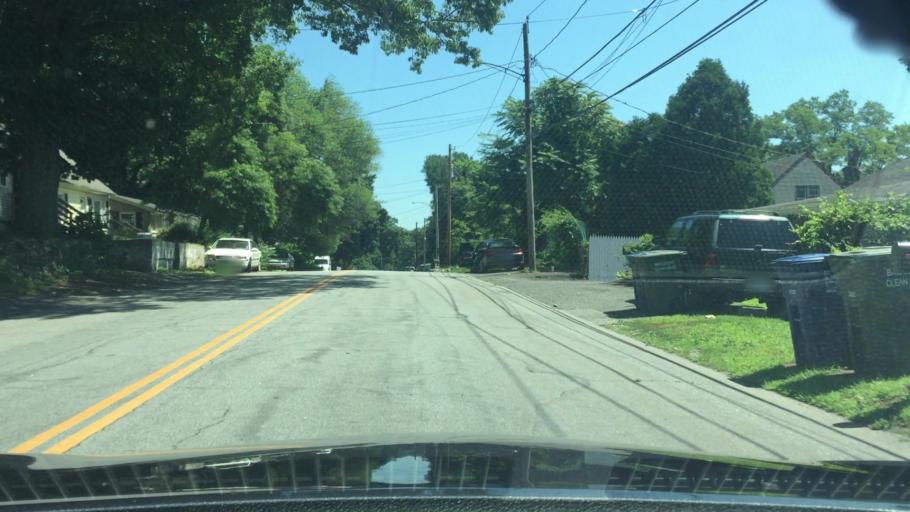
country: US
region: Connecticut
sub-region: Fairfield County
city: Trumbull
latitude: 41.2130
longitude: -73.2073
